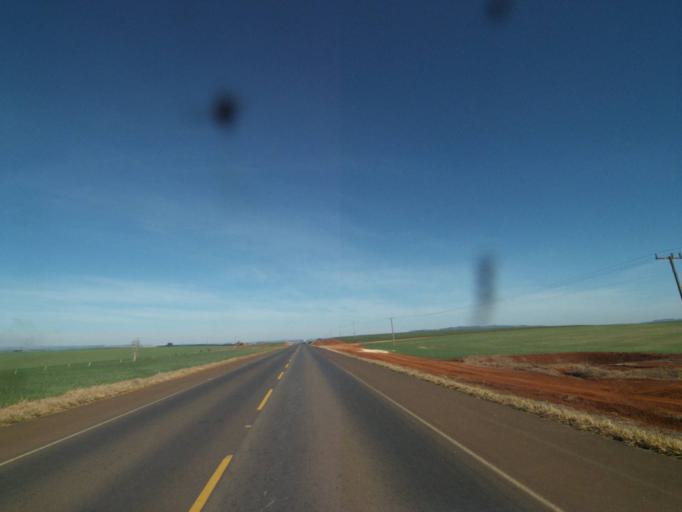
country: BR
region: Parana
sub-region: Tibagi
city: Tibagi
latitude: -24.4460
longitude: -50.4234
